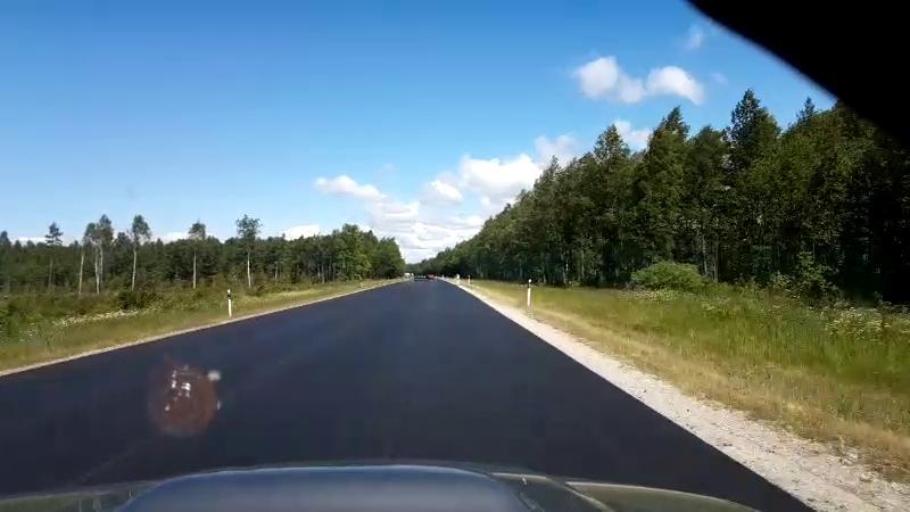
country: LV
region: Salacgrivas
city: Ainazi
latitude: 58.0167
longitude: 24.4960
